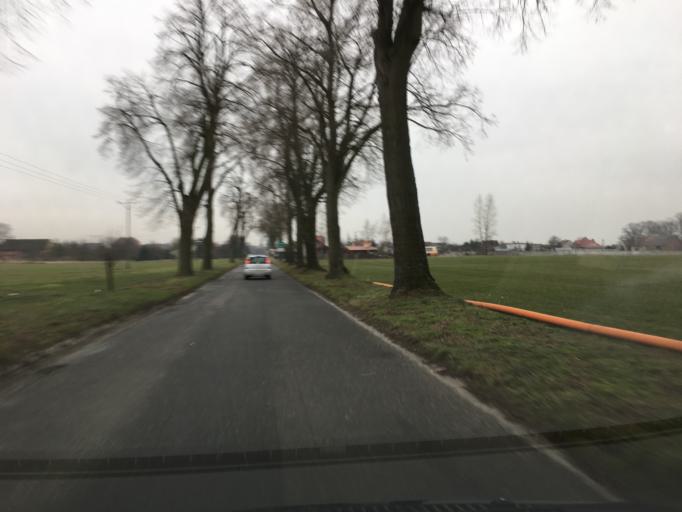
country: PL
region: Opole Voivodeship
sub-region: Powiat kedzierzynsko-kozielski
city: Bierawa
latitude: 50.2890
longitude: 18.2369
